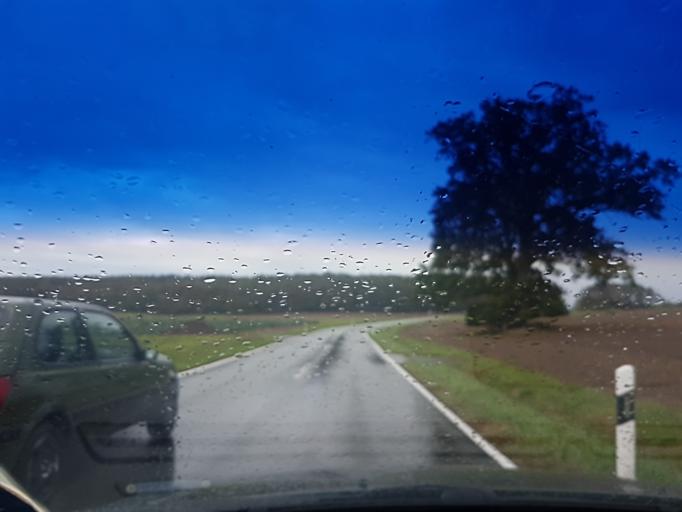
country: DE
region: Bavaria
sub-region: Regierungsbezirk Mittelfranken
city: Wachenroth
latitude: 49.7539
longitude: 10.6662
